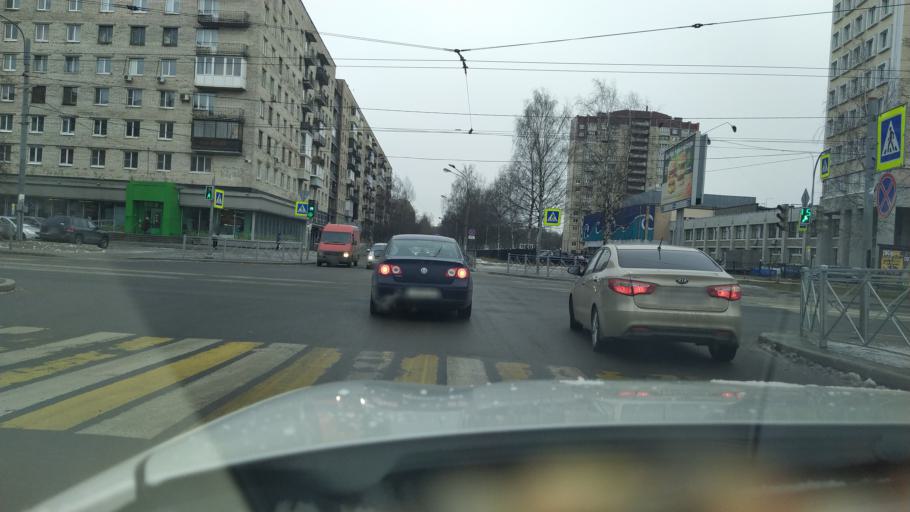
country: RU
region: Leningrad
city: Kalininskiy
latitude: 60.0017
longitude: 30.3860
